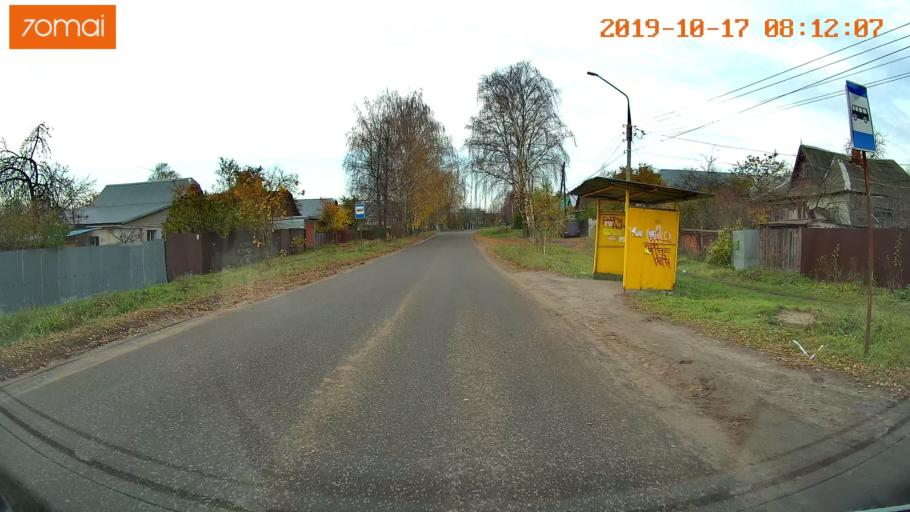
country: RU
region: Vladimir
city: Kol'chugino
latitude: 56.3001
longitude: 39.3617
